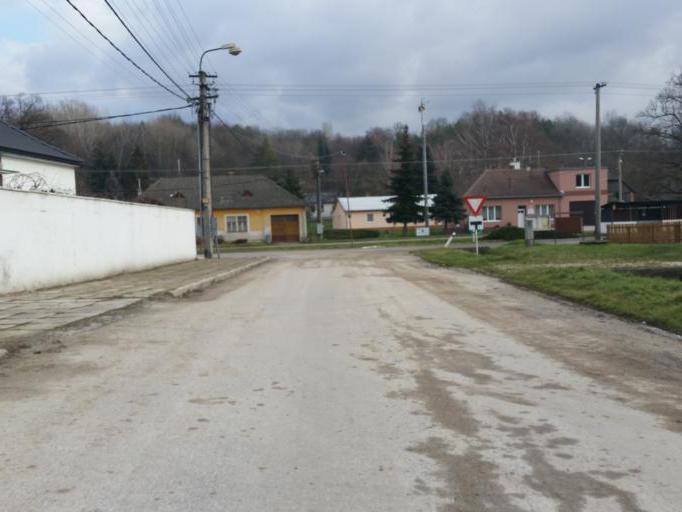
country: SK
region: Trnavsky
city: Vrbove
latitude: 48.6574
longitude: 17.7176
